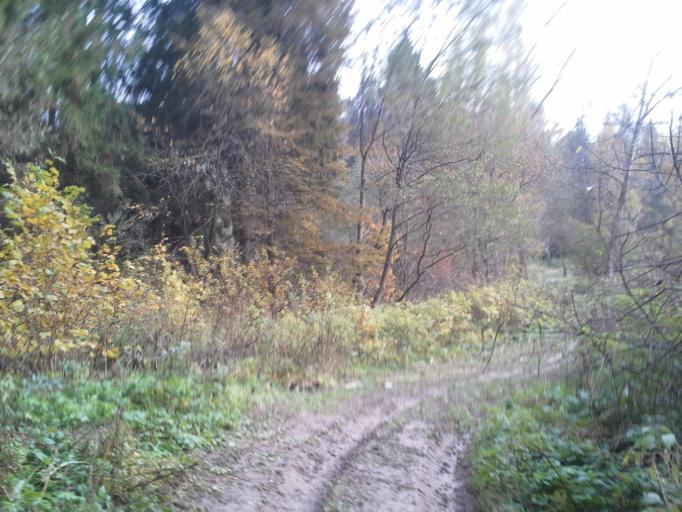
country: RU
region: Moskovskaya
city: Nazar'yevo
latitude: 55.6587
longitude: 37.0167
